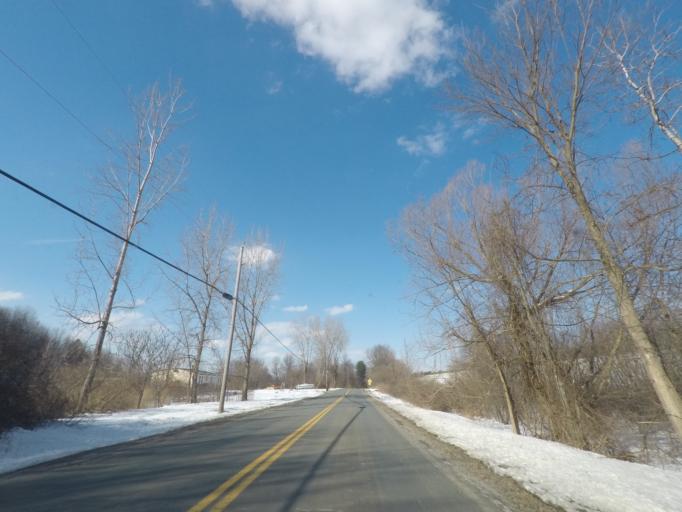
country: US
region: New York
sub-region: Saratoga County
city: Stillwater
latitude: 42.8904
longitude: -73.5705
